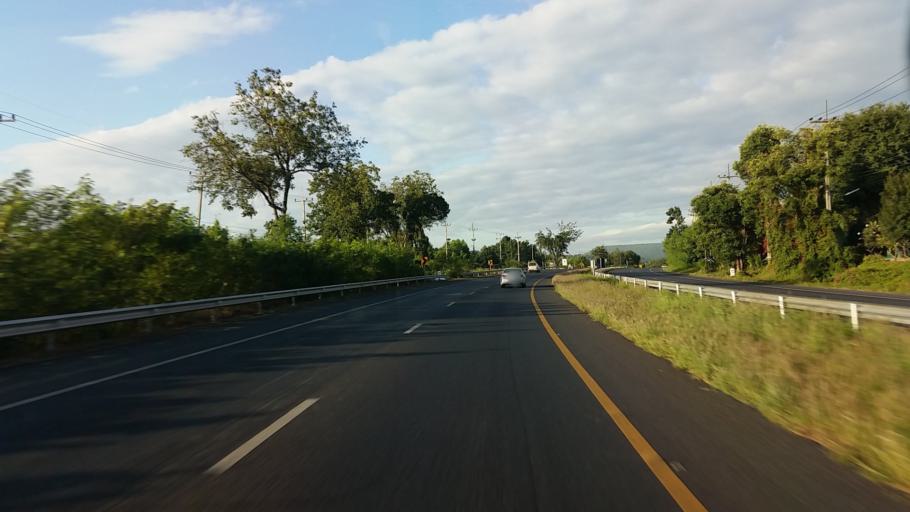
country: TH
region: Lop Buri
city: Phatthana Nikhom
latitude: 14.9894
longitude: 100.9324
